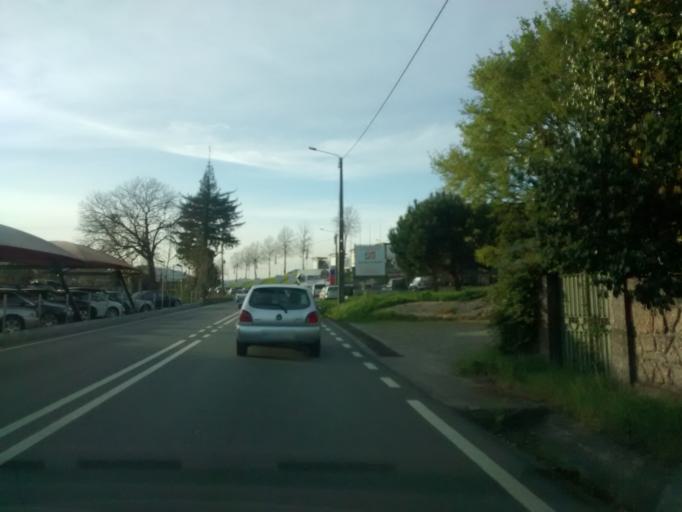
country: PT
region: Braga
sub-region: Guimaraes
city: Ponte
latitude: 41.4737
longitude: -8.3326
